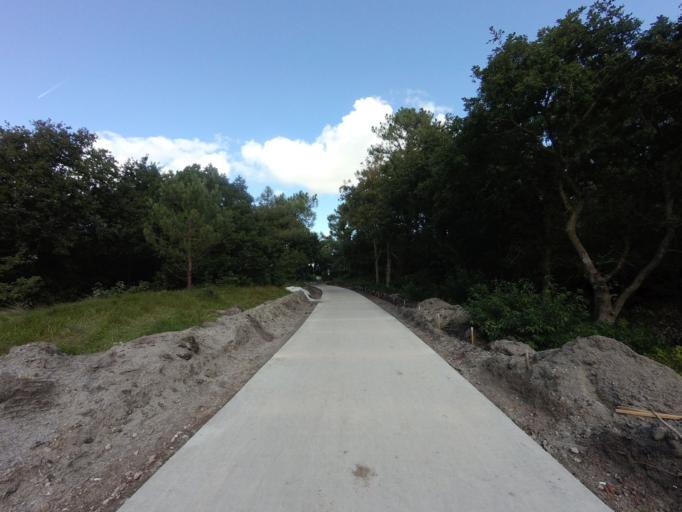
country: NL
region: North Holland
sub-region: Gemeente Bergen
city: Egmond aan Zee
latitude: 52.7200
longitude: 4.6609
